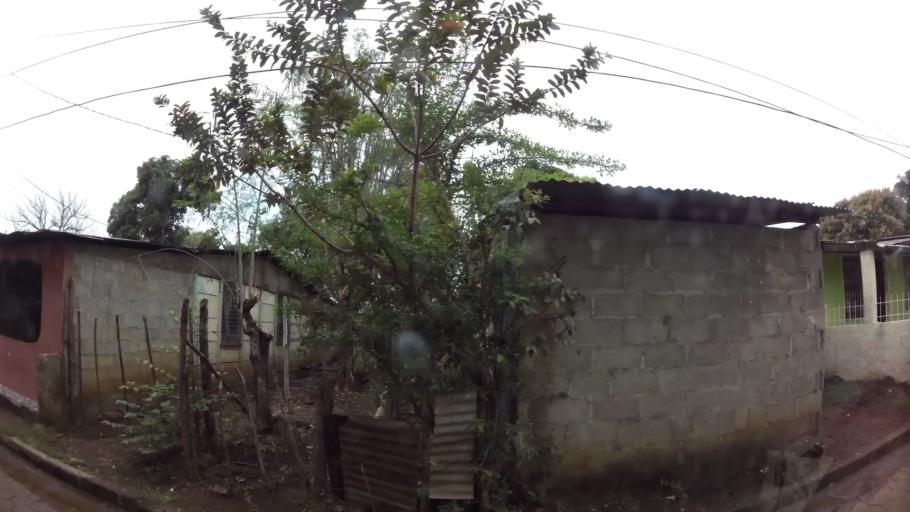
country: NI
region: Granada
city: Nandaime
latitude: 11.7598
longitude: -86.0602
